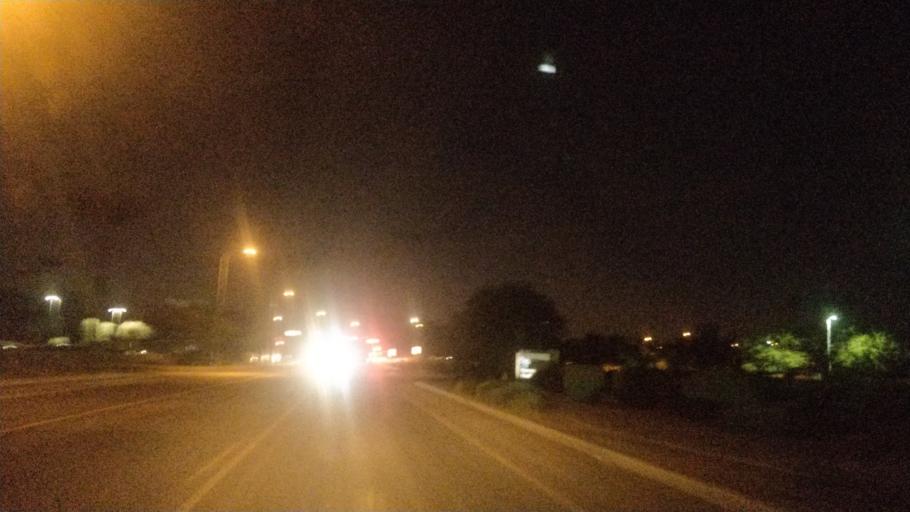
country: US
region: Arizona
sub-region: Maricopa County
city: Chandler
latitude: 33.2838
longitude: -111.8568
